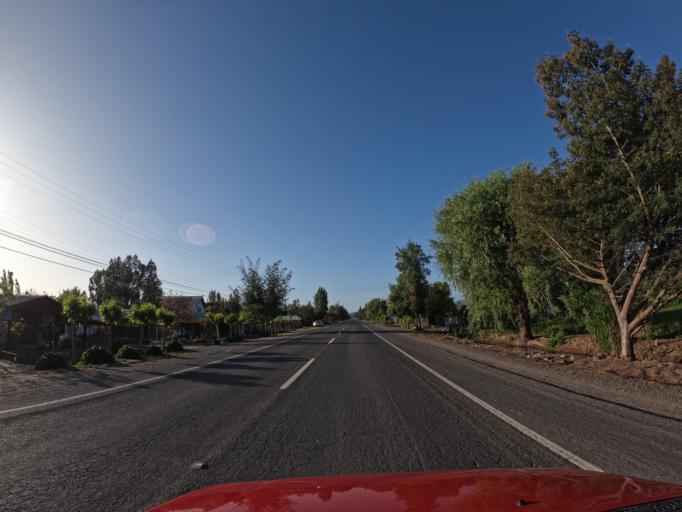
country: CL
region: O'Higgins
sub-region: Provincia de Colchagua
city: Santa Cruz
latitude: -34.4529
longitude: -71.3652
